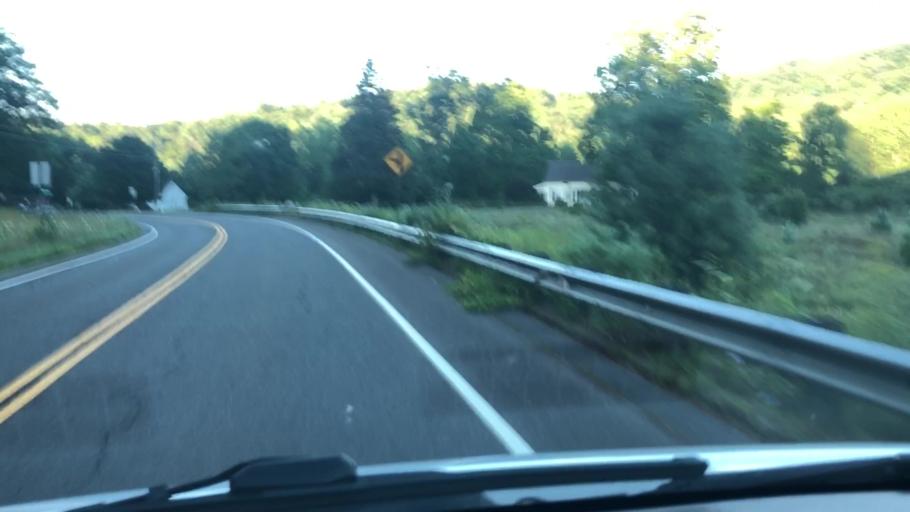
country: US
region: Massachusetts
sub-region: Hampshire County
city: Westhampton
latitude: 42.2809
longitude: -72.8634
